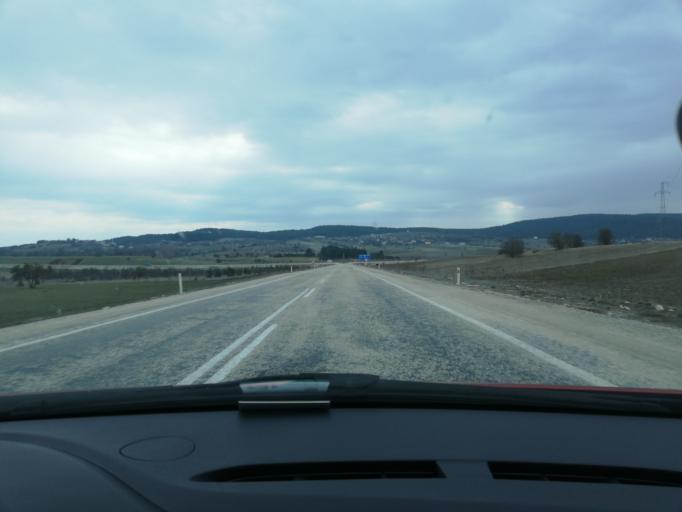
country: TR
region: Karabuk
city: Eflani
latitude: 41.4542
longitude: 33.0407
